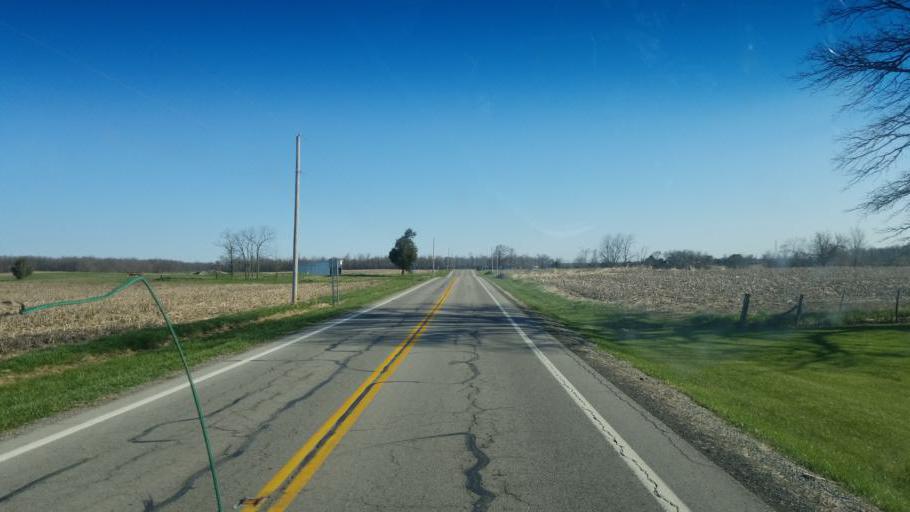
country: US
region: Ohio
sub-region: Logan County
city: Northwood
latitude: 40.5099
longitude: -83.6387
